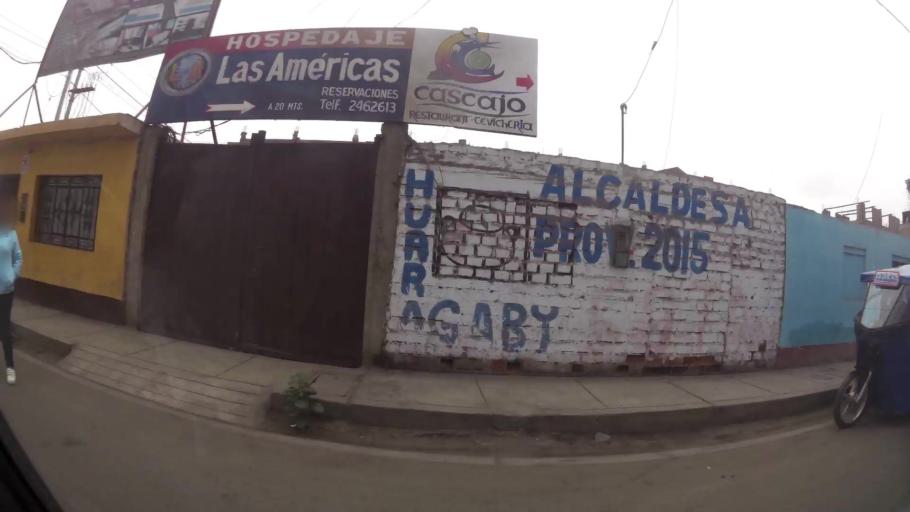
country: PE
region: Lima
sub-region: Provincia de Huaral
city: Huaral
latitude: -11.4930
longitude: -77.2105
